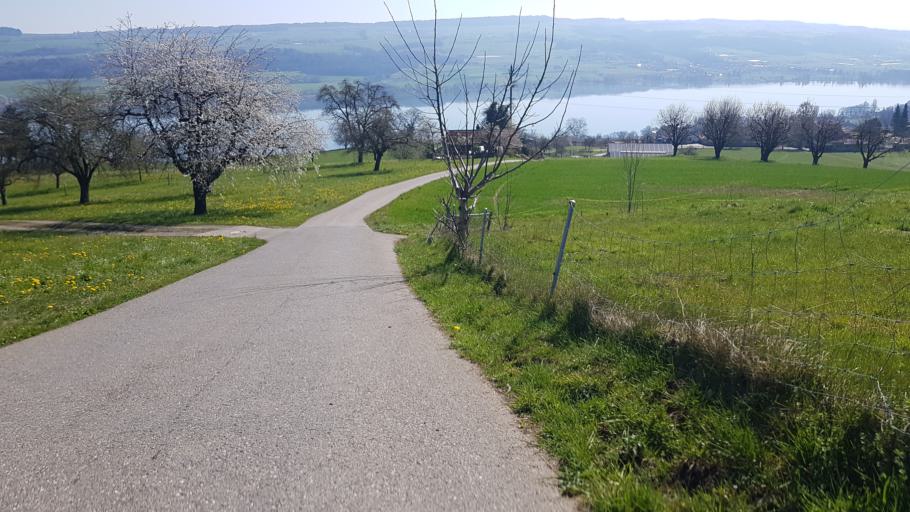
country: CH
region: Aargau
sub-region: Bezirk Kulm
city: Reinach
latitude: 47.2761
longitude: 8.1928
